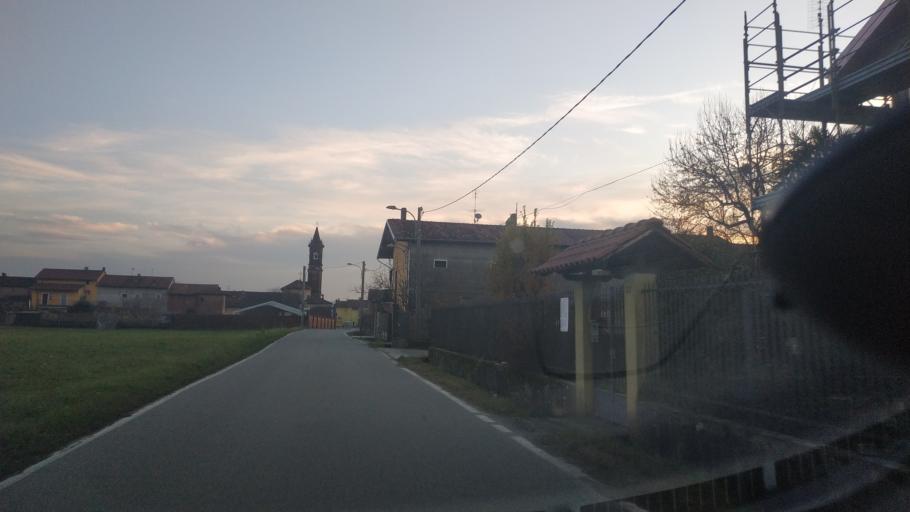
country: IT
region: Piedmont
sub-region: Provincia di Torino
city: Caluso
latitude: 45.2683
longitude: 7.8782
